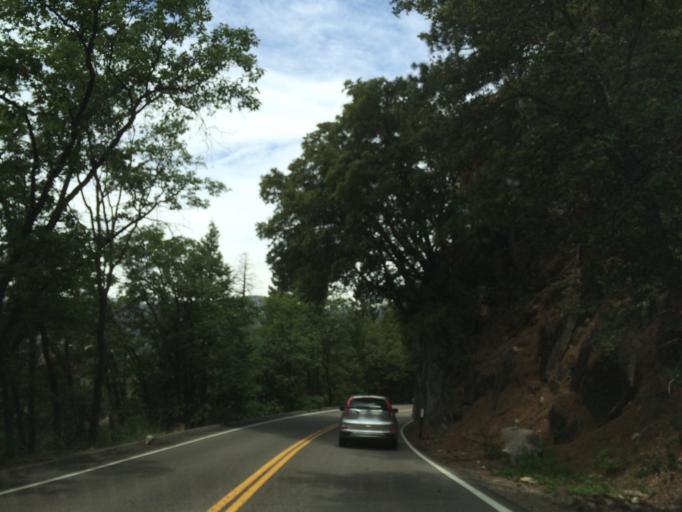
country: US
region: California
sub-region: Mariposa County
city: Yosemite Valley
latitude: 37.7058
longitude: -119.7115
